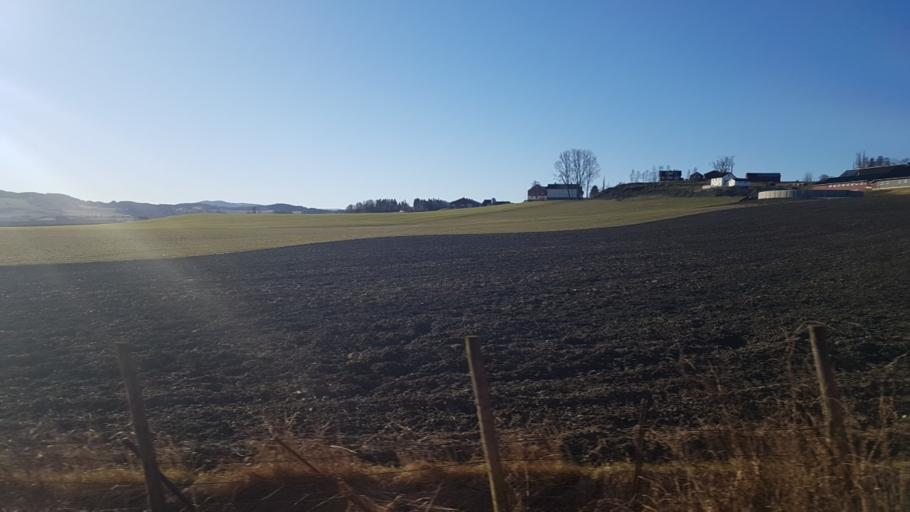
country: NO
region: Nord-Trondelag
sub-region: Levanger
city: Skogn
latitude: 63.6940
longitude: 11.1790
